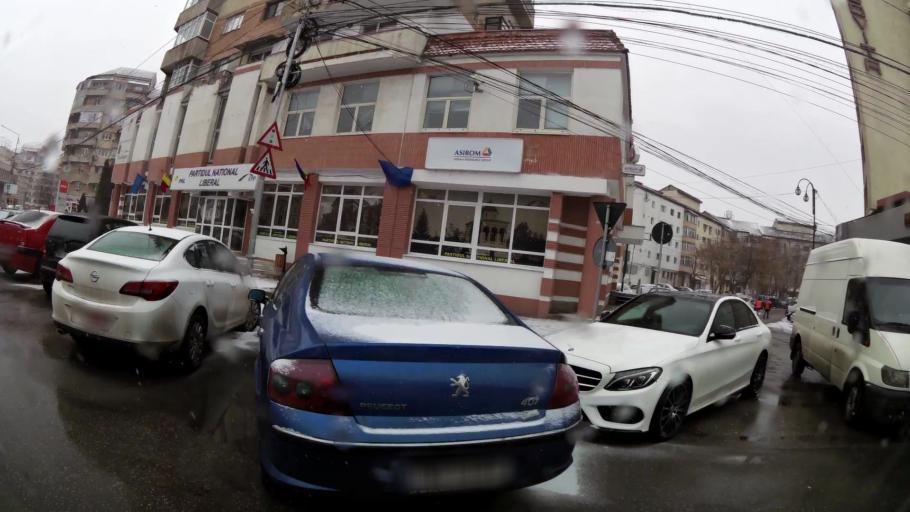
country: RO
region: Dambovita
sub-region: Municipiul Targoviste
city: Targoviste
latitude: 44.9263
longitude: 25.4592
